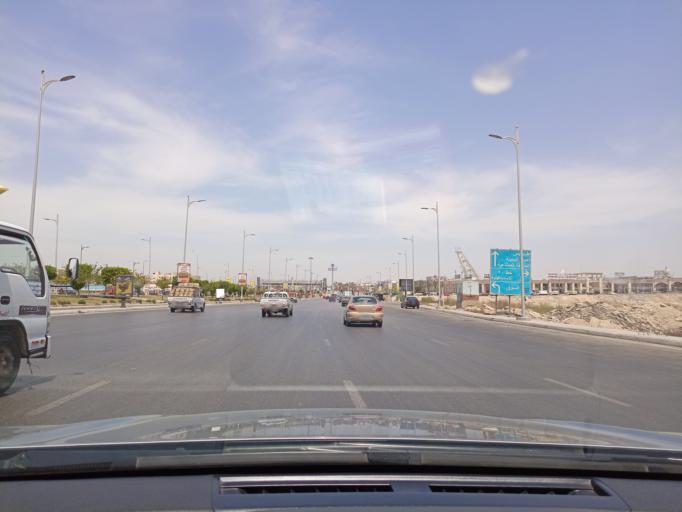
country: EG
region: Muhafazat al Qalyubiyah
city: Al Khankah
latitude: 30.1682
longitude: 31.4770
